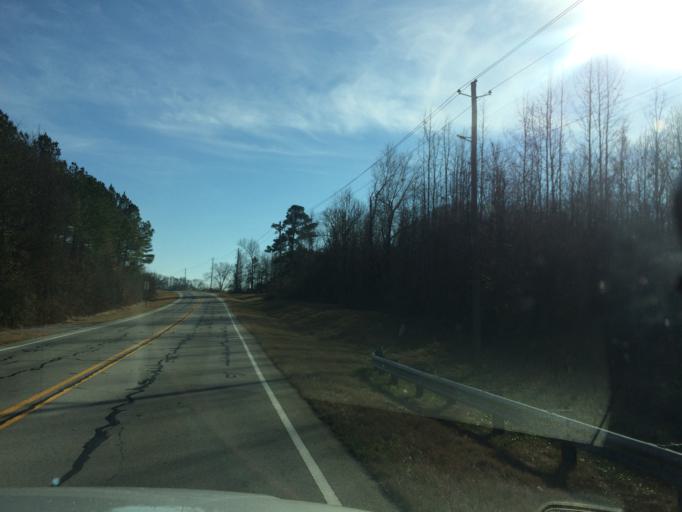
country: US
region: Georgia
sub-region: Franklin County
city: Gumlog
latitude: 34.4661
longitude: -83.0585
